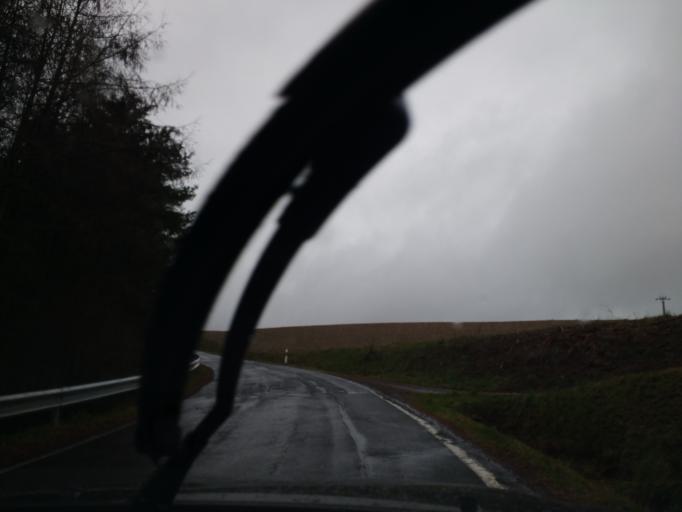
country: DE
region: Rheinland-Pfalz
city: Rascheid
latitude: 49.7238
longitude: 6.9284
